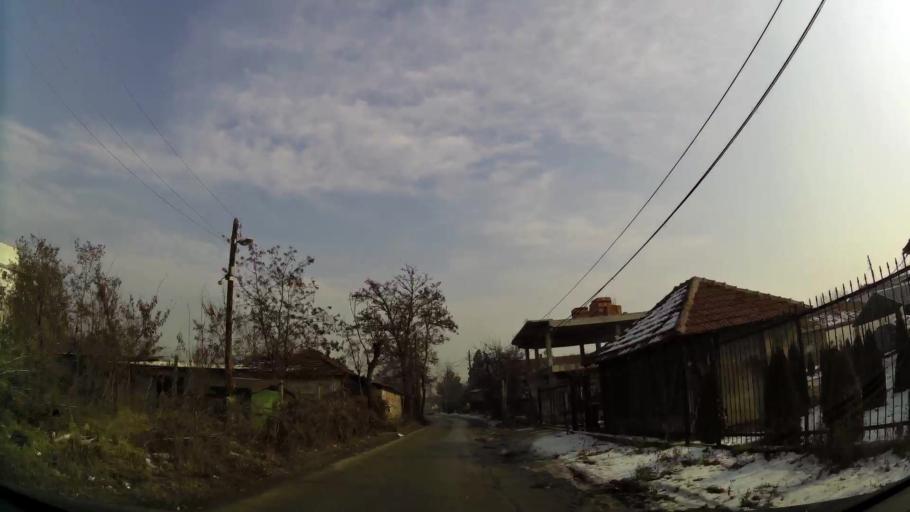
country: MK
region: Kisela Voda
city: Kisela Voda
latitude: 41.9965
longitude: 21.4960
